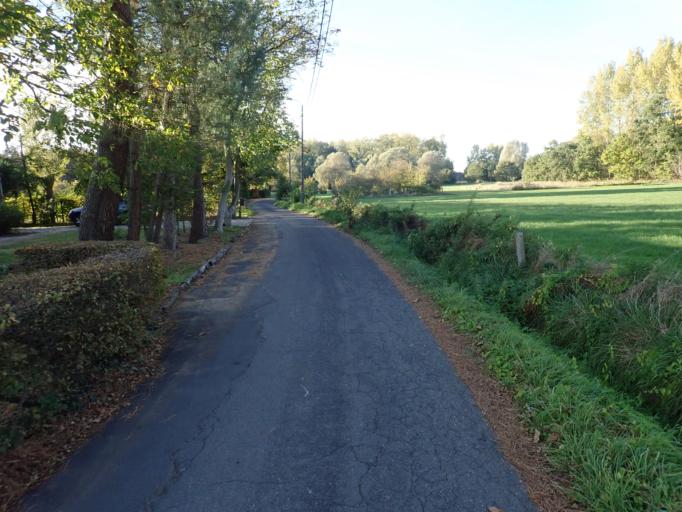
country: BE
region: Flanders
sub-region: Provincie Antwerpen
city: Putte
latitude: 51.0287
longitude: 4.5989
